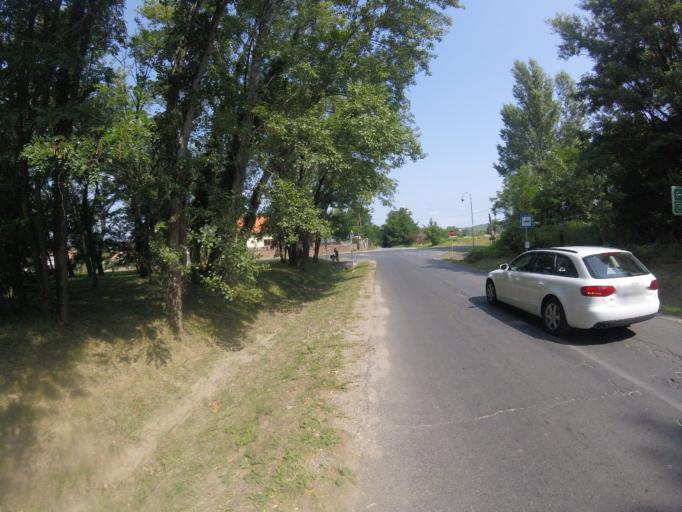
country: HU
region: Veszprem
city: Tapolca
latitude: 46.8077
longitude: 17.4348
